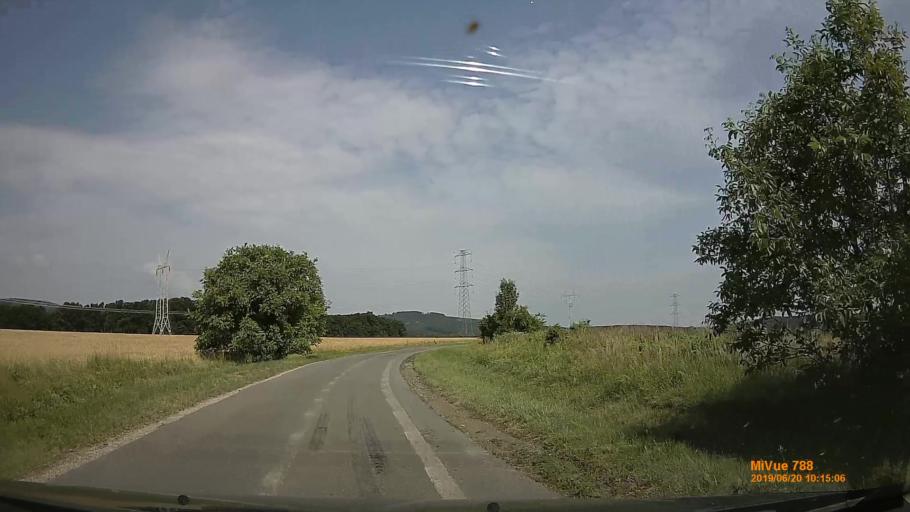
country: HU
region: Baranya
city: Mecseknadasd
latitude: 46.1891
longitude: 18.4665
